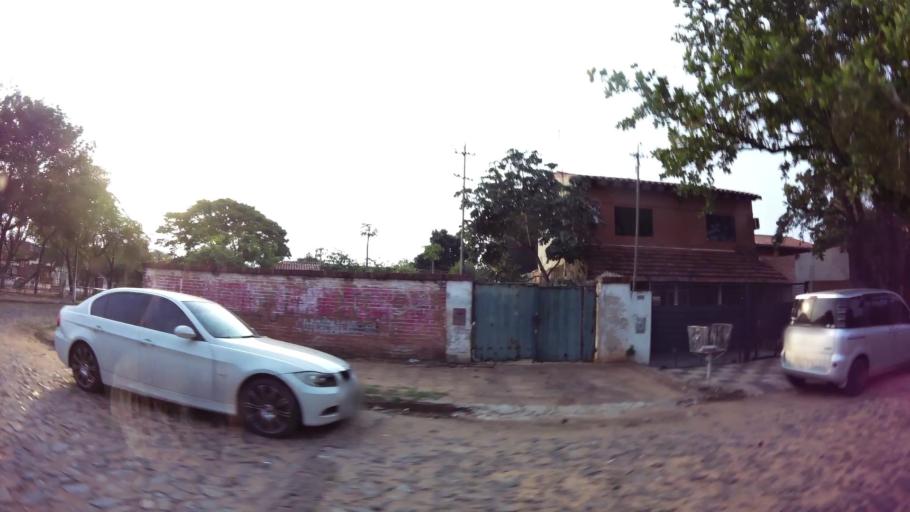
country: PY
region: Central
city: Lambare
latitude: -25.3180
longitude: -57.5765
